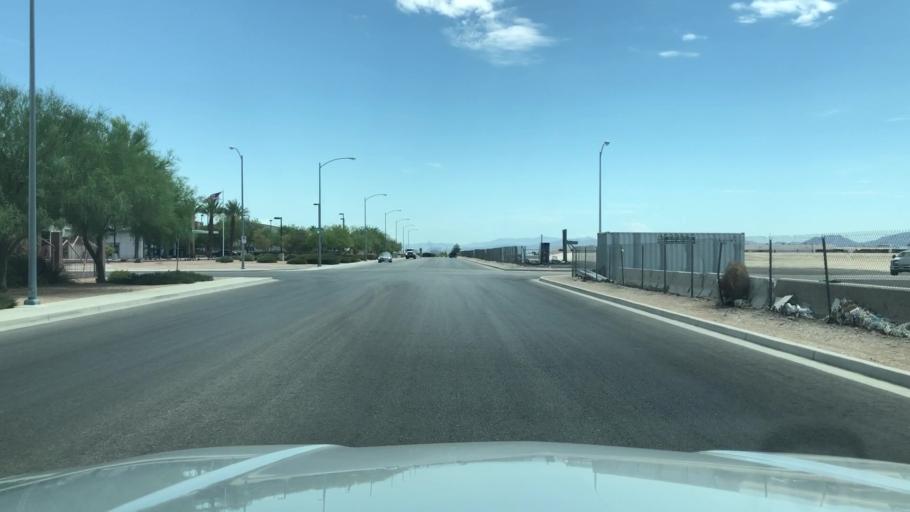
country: US
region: Nevada
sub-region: Clark County
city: Spring Valley
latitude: 36.0827
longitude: -115.2045
